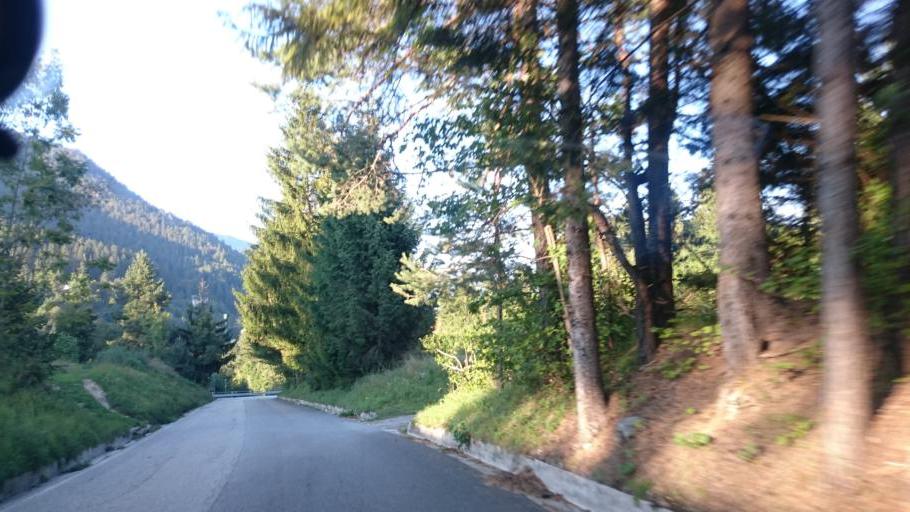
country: IT
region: Friuli Venezia Giulia
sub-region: Provincia di Udine
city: Tarvisio
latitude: 46.5010
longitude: 13.5921
